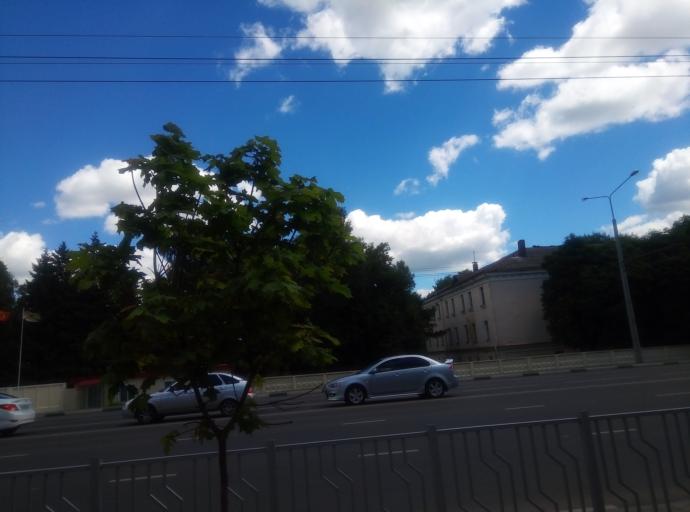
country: RU
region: Kursk
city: Kursk
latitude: 51.7629
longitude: 36.1847
